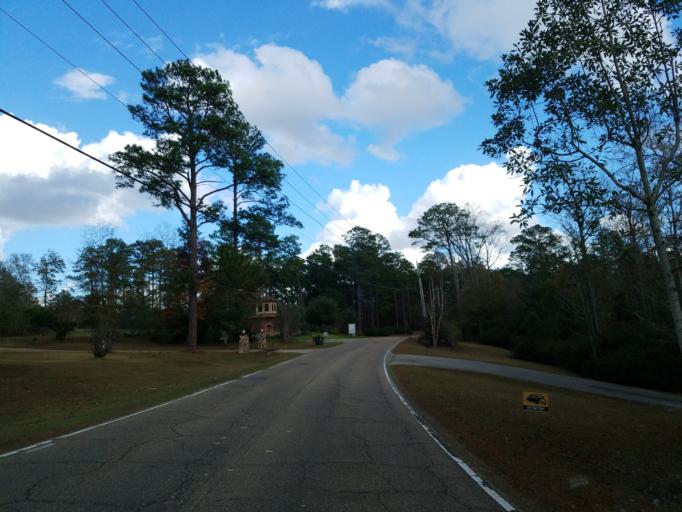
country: US
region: Mississippi
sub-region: Lamar County
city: West Hattiesburg
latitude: 31.2854
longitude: -89.3400
